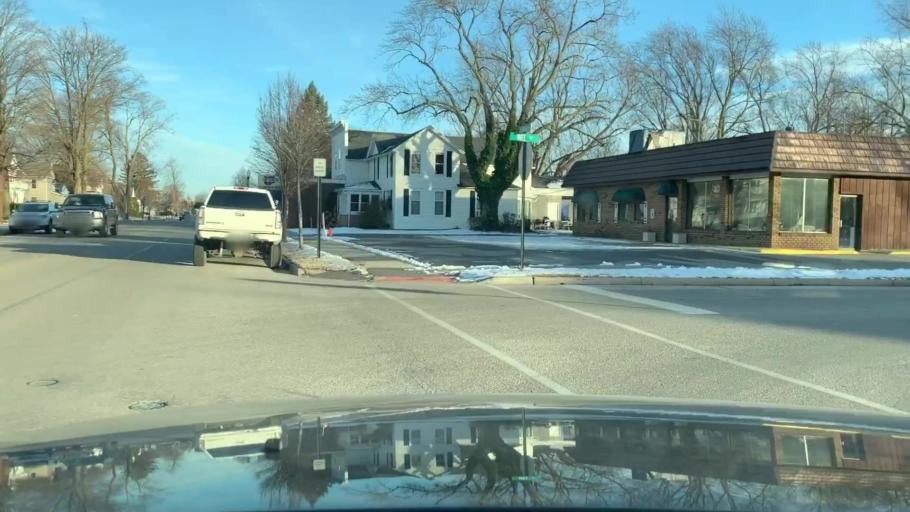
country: US
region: Michigan
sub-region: Ottawa County
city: Zeeland
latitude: 42.8123
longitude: -86.0248
